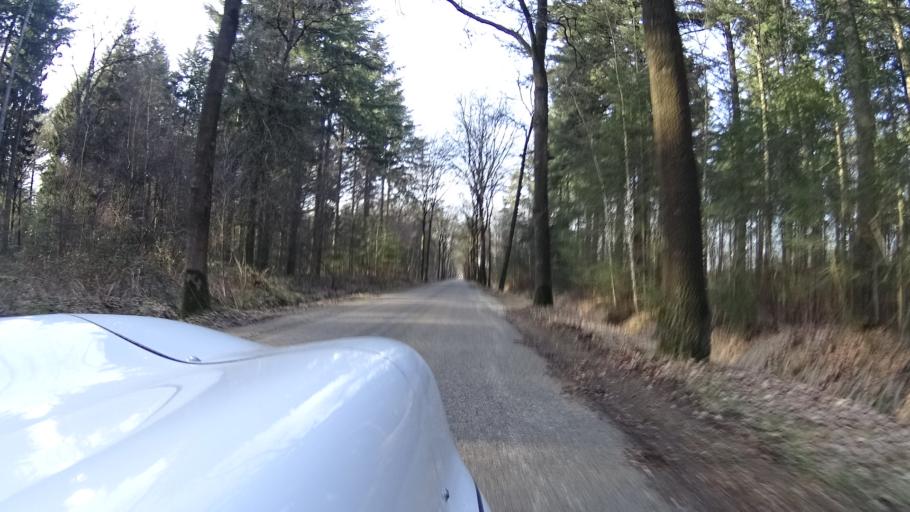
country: NL
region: North Brabant
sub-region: Gemeente Veghel
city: Erp
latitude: 51.5704
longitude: 5.6330
